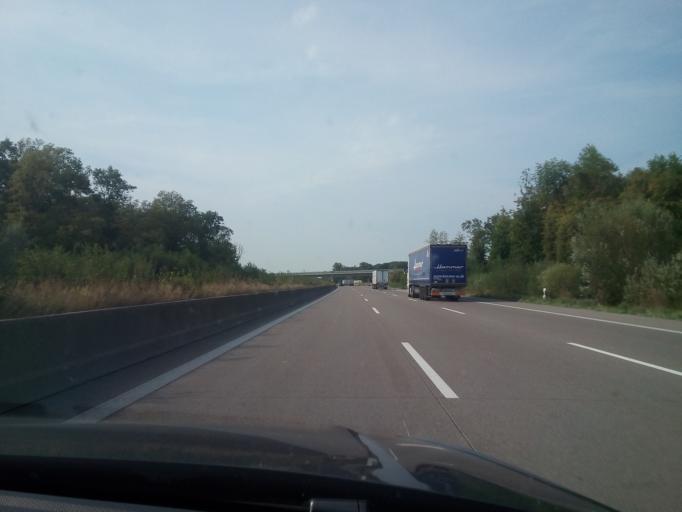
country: DE
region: Baden-Wuerttemberg
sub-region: Freiburg Region
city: Willstatt
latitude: 48.5036
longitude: 7.9059
